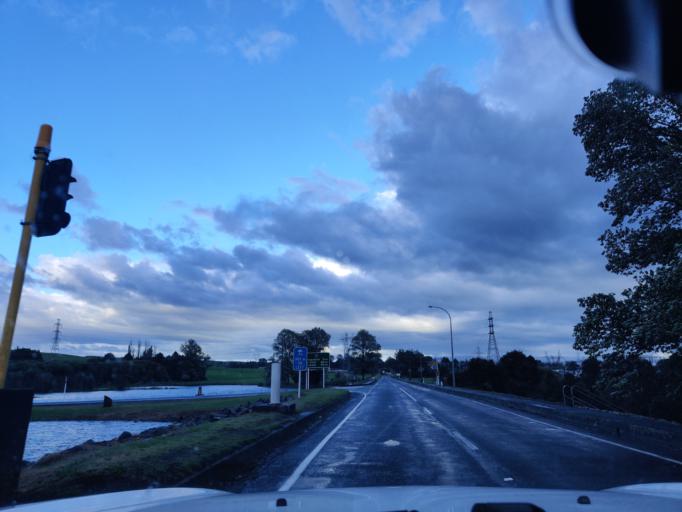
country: NZ
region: Waikato
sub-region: South Waikato District
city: Tokoroa
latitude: -38.4205
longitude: 175.8063
